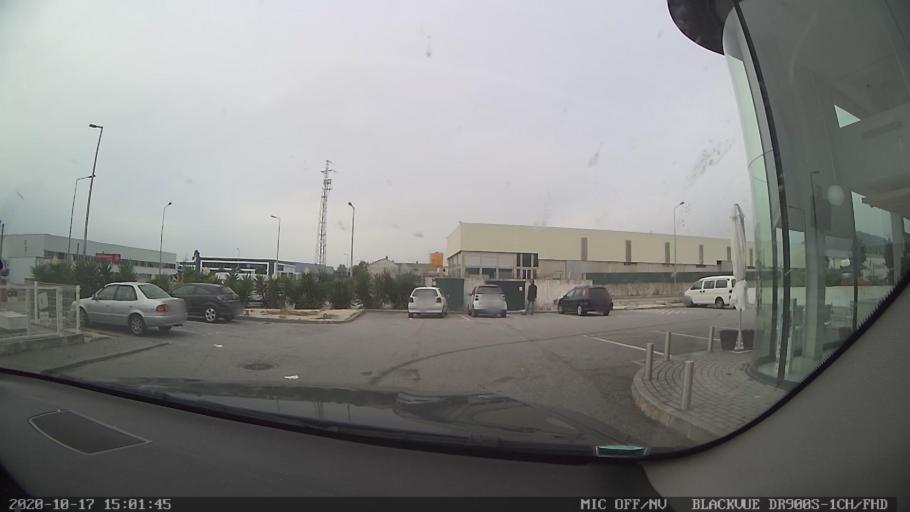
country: PT
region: Braga
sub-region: Esposende
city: Esposende
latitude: 41.5302
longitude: -8.7630
